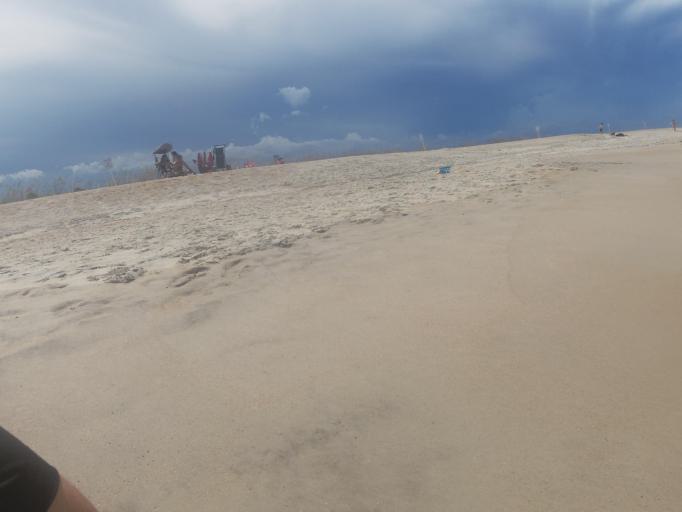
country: US
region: Florida
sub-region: Saint Johns County
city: Saint Augustine Beach
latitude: 29.8638
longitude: -81.2666
